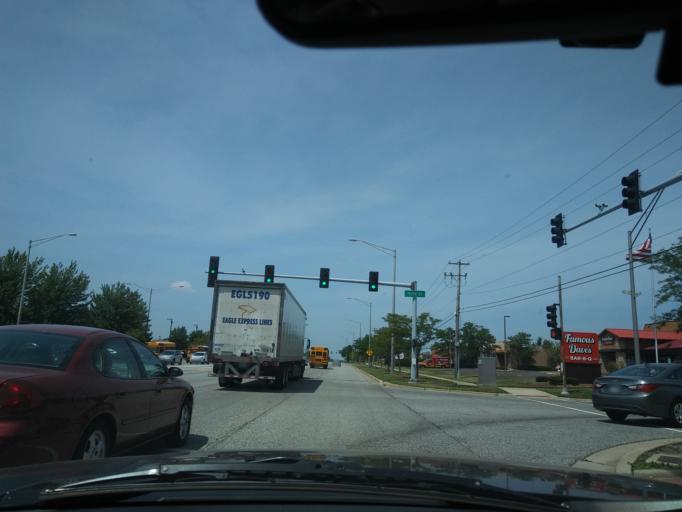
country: US
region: Illinois
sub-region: Cook County
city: Tinley Park
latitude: 41.6057
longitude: -87.7941
